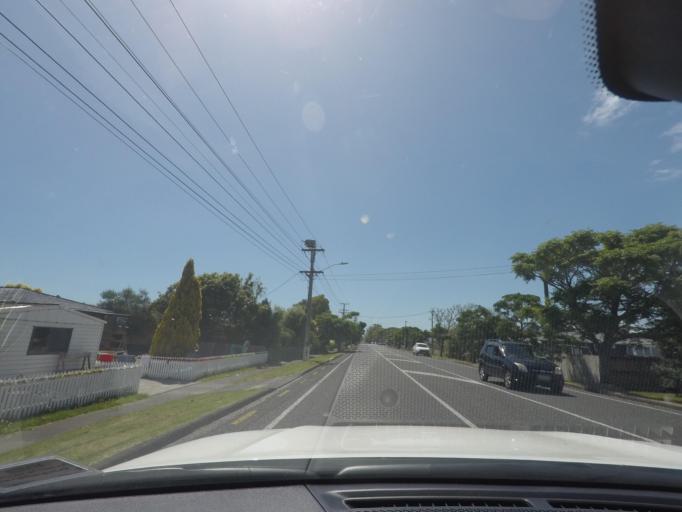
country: NZ
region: Auckland
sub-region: Auckland
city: Parakai
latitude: -36.6631
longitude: 174.4357
